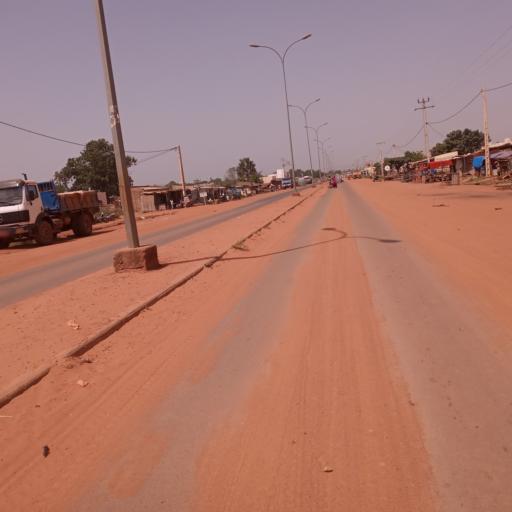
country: ML
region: Bamako
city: Bamako
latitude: 12.4795
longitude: -8.0559
